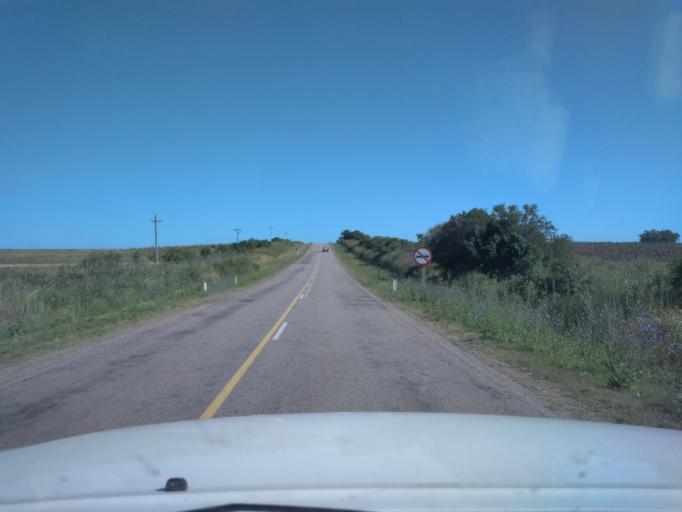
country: UY
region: Canelones
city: San Ramon
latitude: -34.1812
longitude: -55.9414
